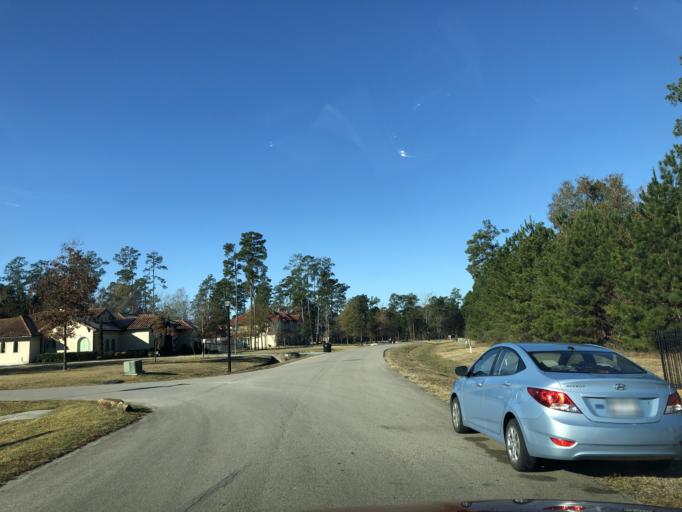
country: US
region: Texas
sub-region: Montgomery County
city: Porter Heights
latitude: 30.0700
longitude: -95.3222
